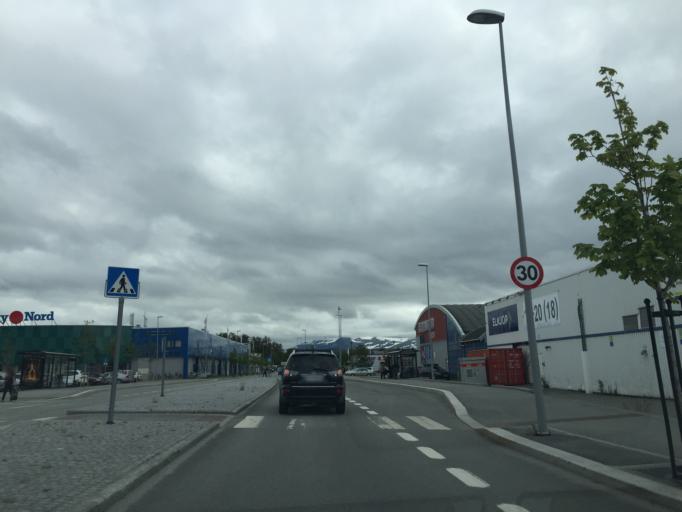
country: NO
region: Nordland
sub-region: Bodo
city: Bodo
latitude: 67.2775
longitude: 14.4195
